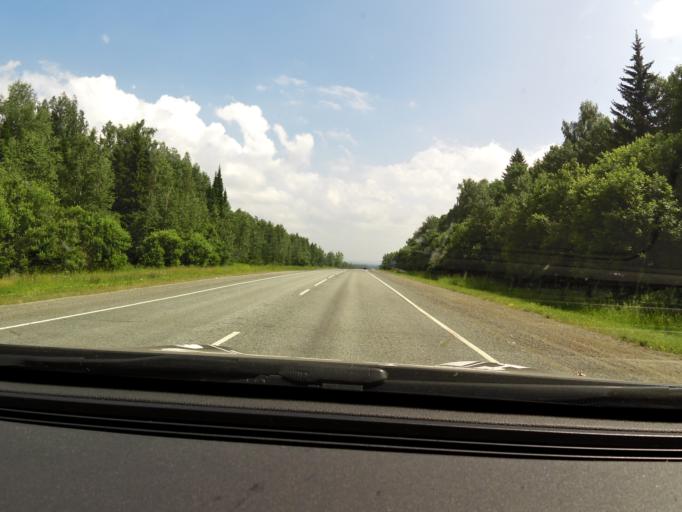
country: RU
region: Sverdlovsk
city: Achit
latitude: 56.8275
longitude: 57.7940
